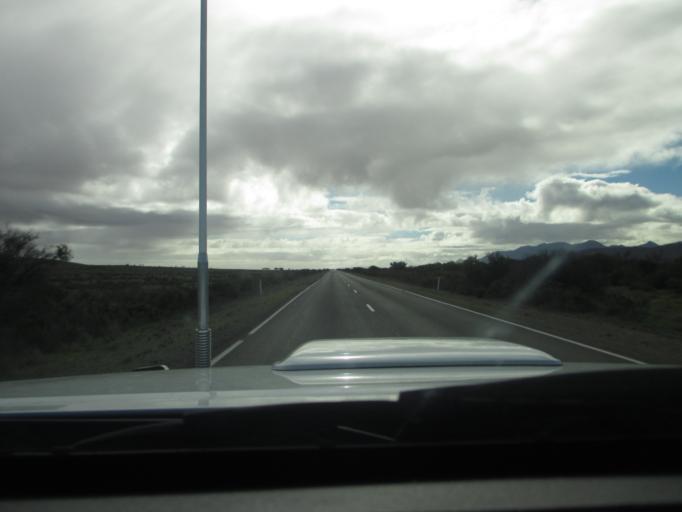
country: AU
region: South Australia
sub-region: Flinders Ranges
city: Quorn
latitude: -31.6410
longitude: 138.3842
